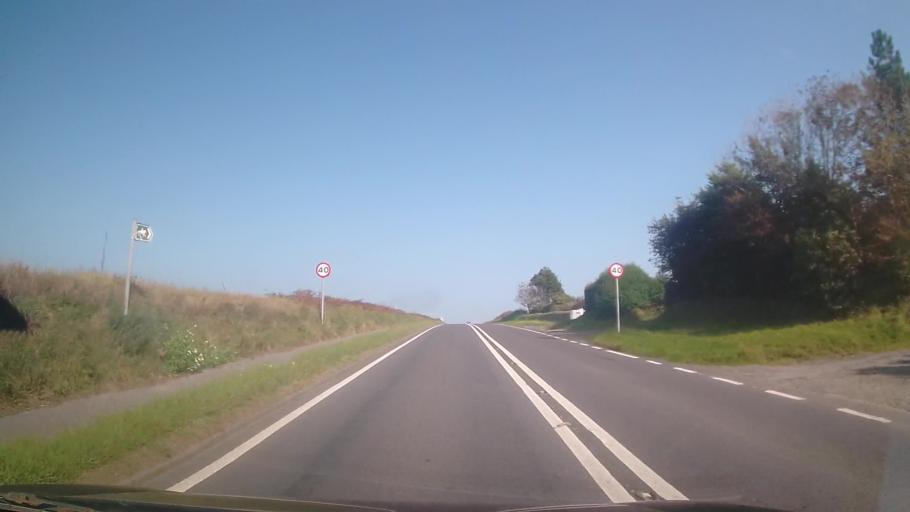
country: GB
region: Wales
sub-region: County of Ceredigion
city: Aberporth
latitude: 52.1041
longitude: -4.5998
